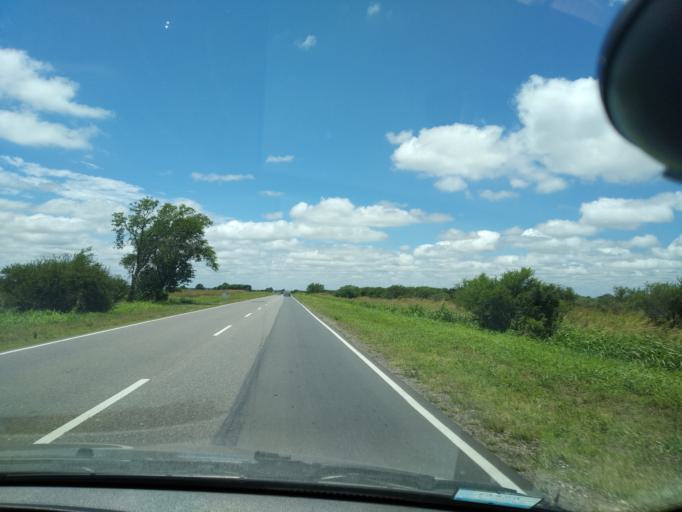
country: AR
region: Cordoba
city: Despenaderos
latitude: -31.6518
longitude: -64.2044
